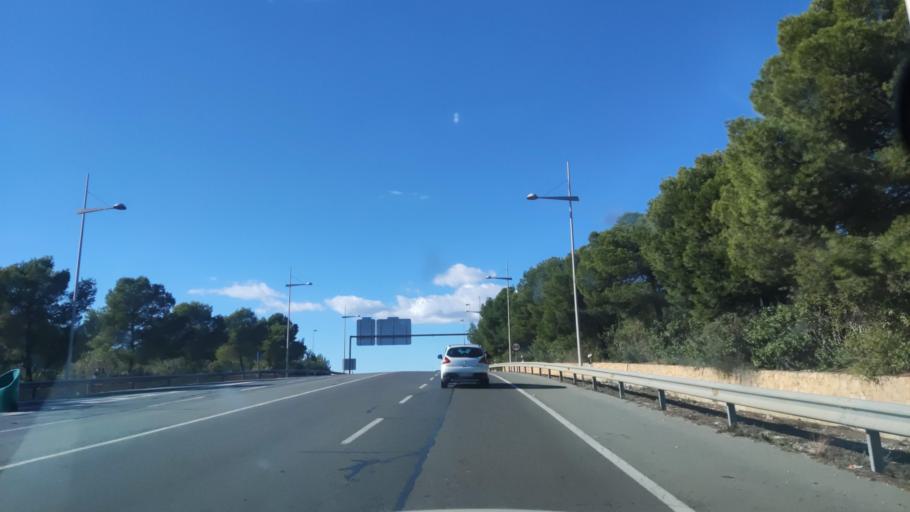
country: ES
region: Valencia
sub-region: Provincia de Alicante
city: Benidorm
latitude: 38.5492
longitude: -0.1654
